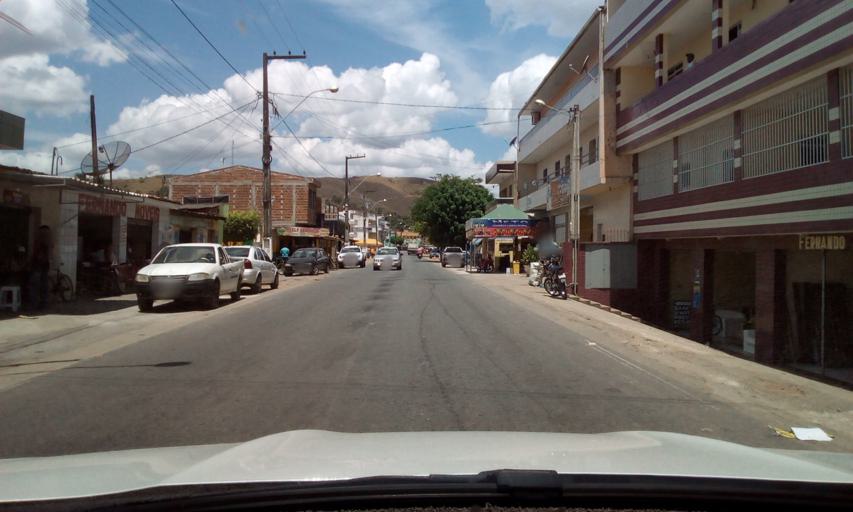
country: BR
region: Paraiba
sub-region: Alagoinha
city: Alagoinha
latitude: -6.9522
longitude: -35.5450
